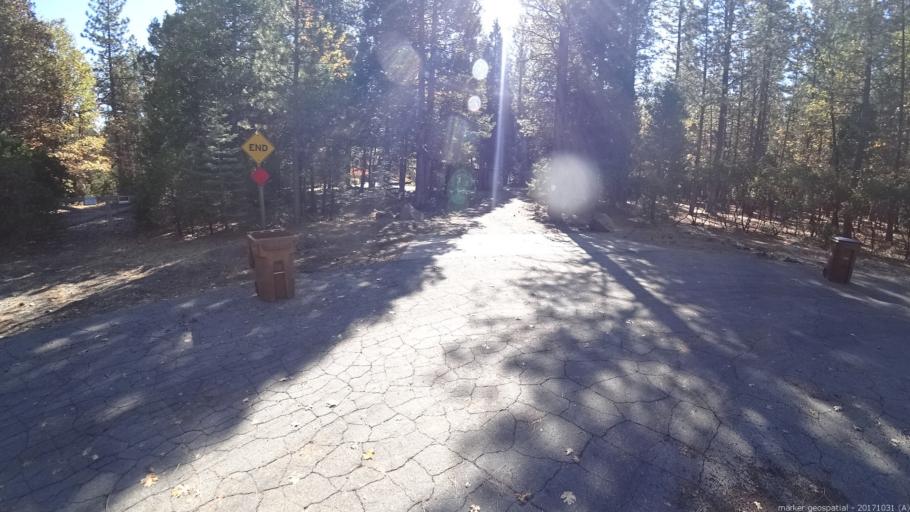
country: US
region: California
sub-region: Shasta County
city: Shingletown
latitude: 40.4839
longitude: -121.8839
